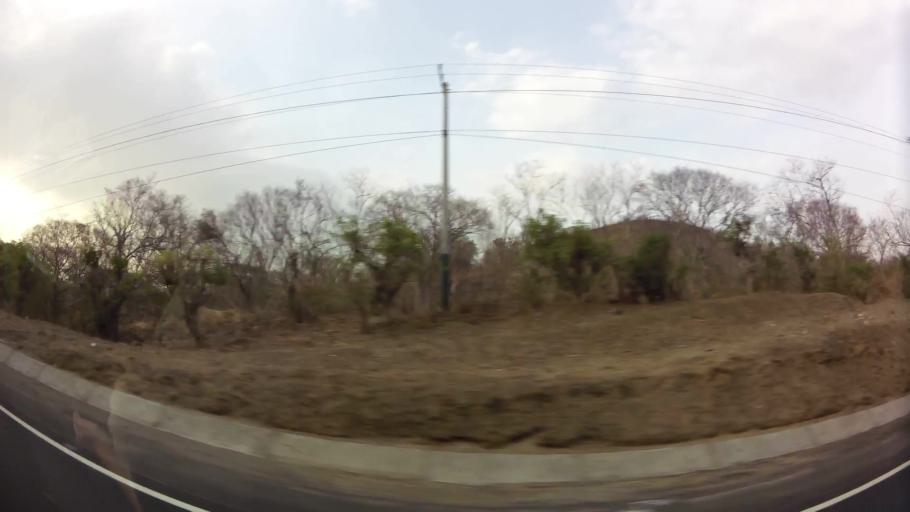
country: NI
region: Leon
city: Nagarote
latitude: 12.2563
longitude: -86.4581
